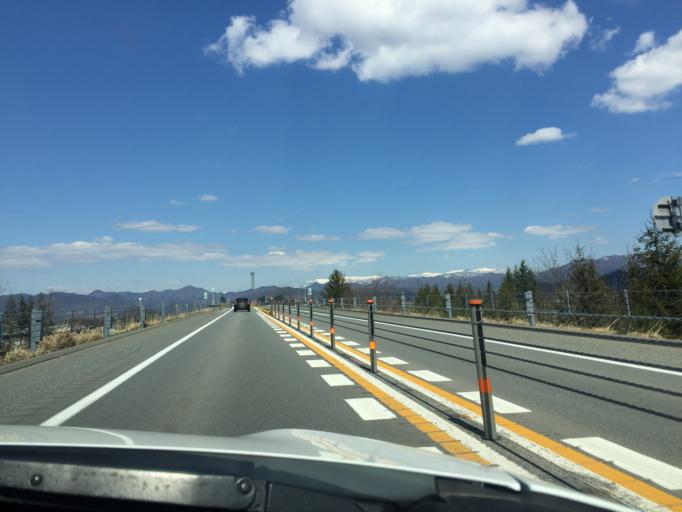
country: JP
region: Yamagata
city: Takahata
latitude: 37.9838
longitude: 140.1508
